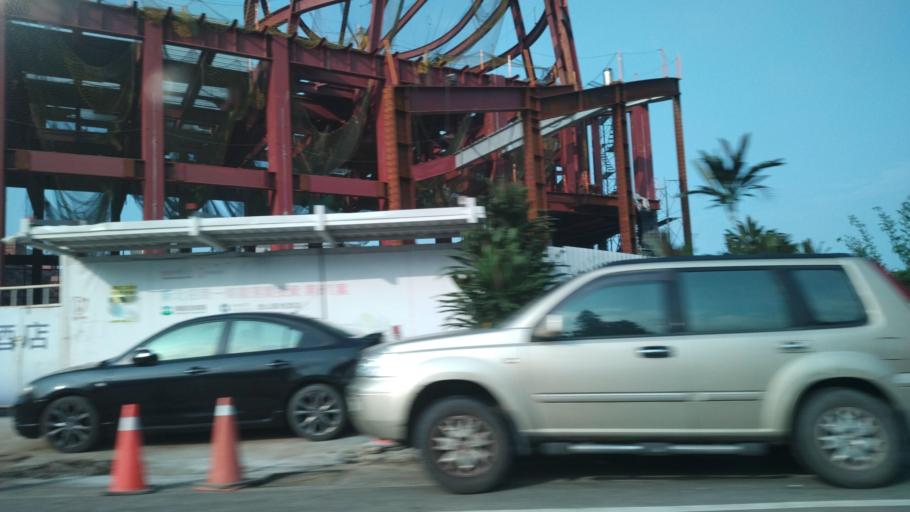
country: TW
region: Taiwan
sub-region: Keelung
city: Keelung
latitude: 25.2178
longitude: 121.6341
